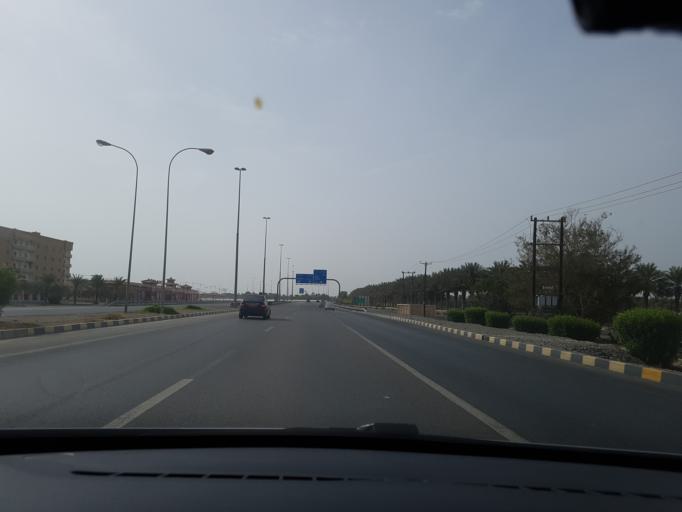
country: OM
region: Al Batinah
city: Al Sohar
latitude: 24.3505
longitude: 56.7150
